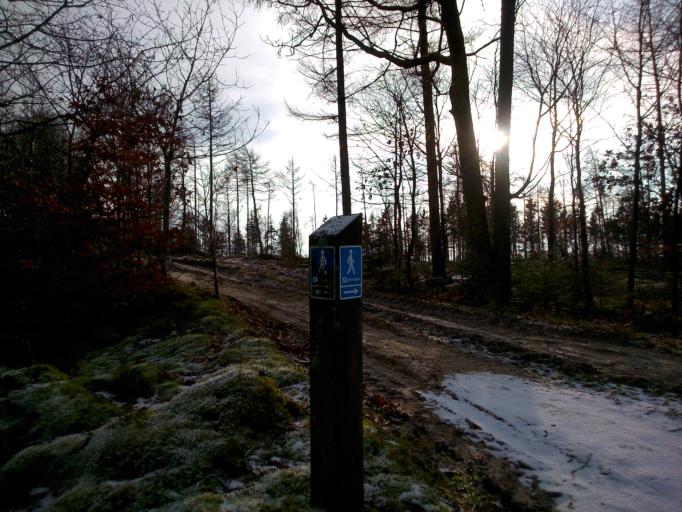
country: DK
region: Central Jutland
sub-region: Ringkobing-Skjern Kommune
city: Skjern
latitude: 55.9999
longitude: 8.4293
